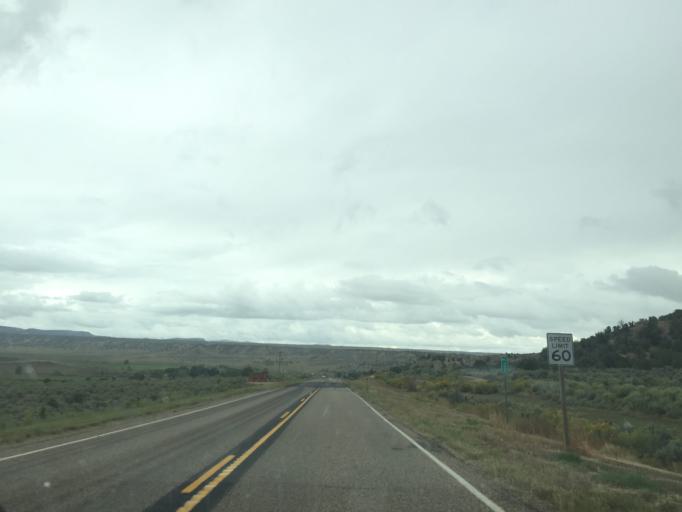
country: US
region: Utah
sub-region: Garfield County
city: Panguitch
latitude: 37.6140
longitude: -112.0728
